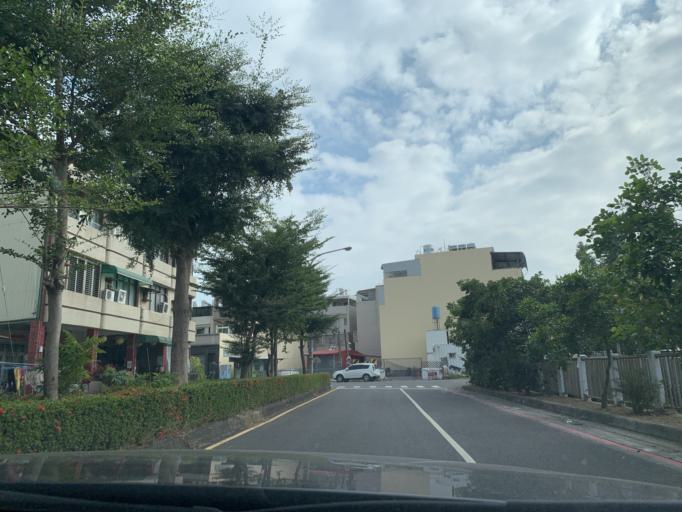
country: TW
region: Taiwan
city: Fengshan
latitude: 22.4672
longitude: 120.4559
